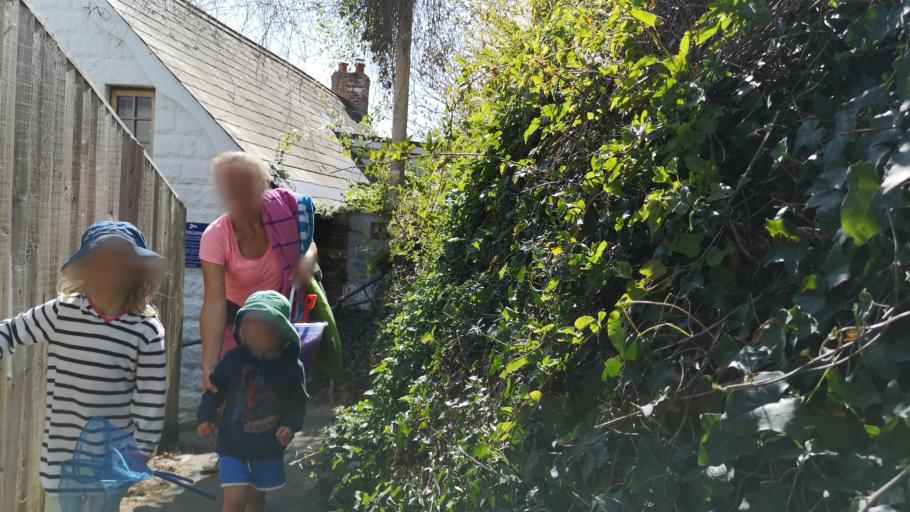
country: GB
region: England
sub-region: Isle of Wight
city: Ventnor
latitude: 50.5890
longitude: -1.2243
